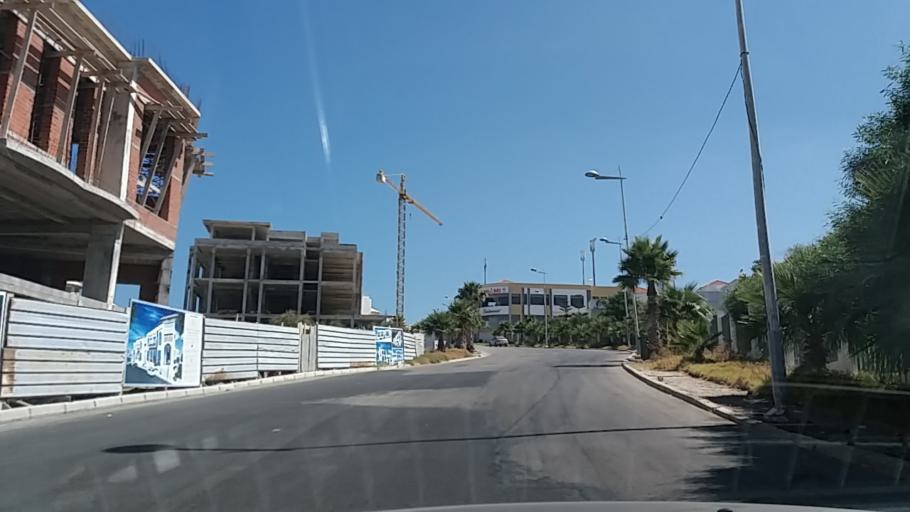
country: MA
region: Tanger-Tetouan
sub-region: Tanger-Assilah
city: Tangier
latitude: 35.7894
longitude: -5.7563
